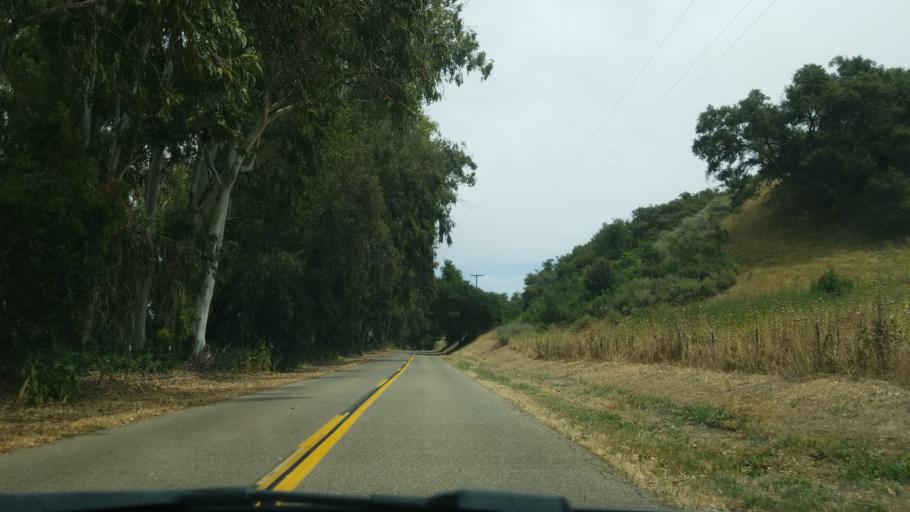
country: US
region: California
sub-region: Santa Barbara County
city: Los Olivos
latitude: 34.7803
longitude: -120.1596
